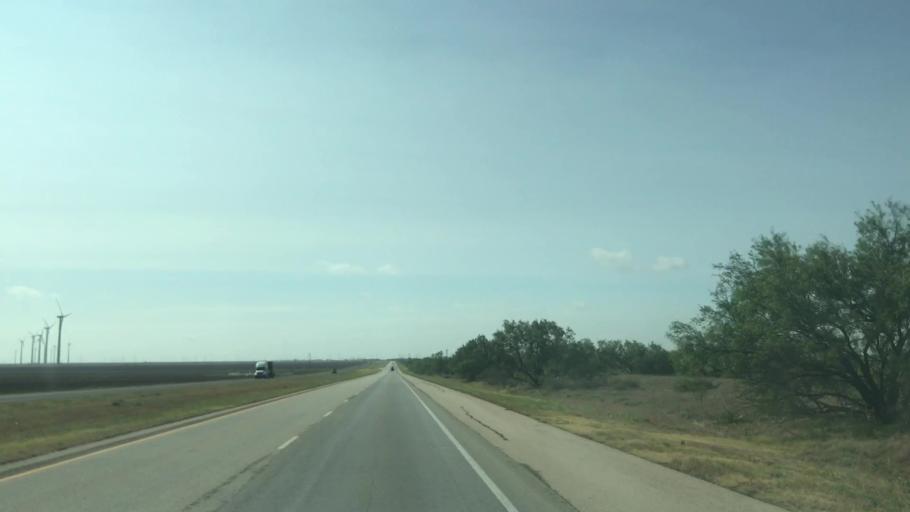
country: US
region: Texas
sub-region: Scurry County
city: Snyder
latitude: 32.5934
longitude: -100.7343
